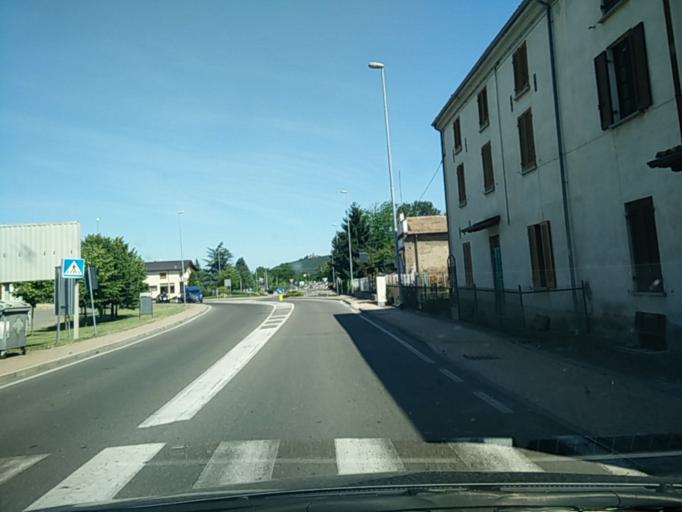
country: IT
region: Lombardy
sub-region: Provincia di Pavia
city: Godiasco
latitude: 44.8986
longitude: 9.0538
